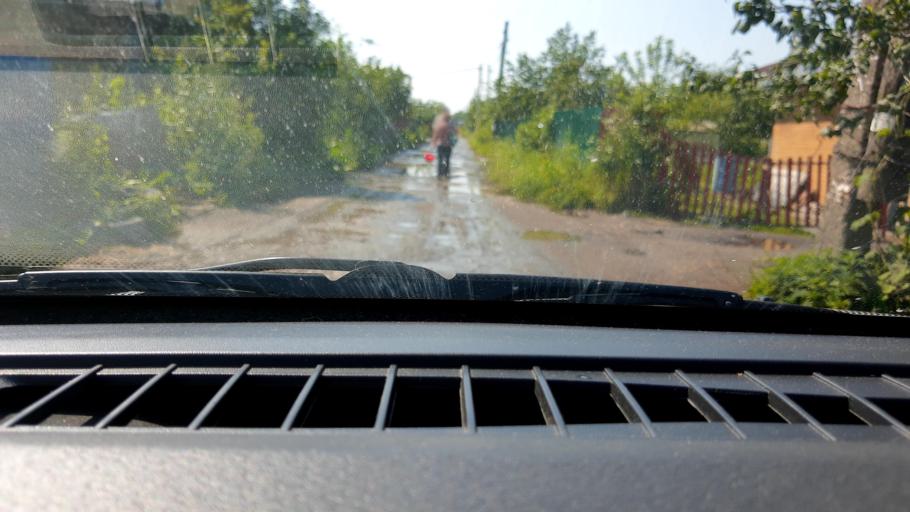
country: RU
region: Nizjnij Novgorod
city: Gorbatovka
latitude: 56.3166
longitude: 43.8297
